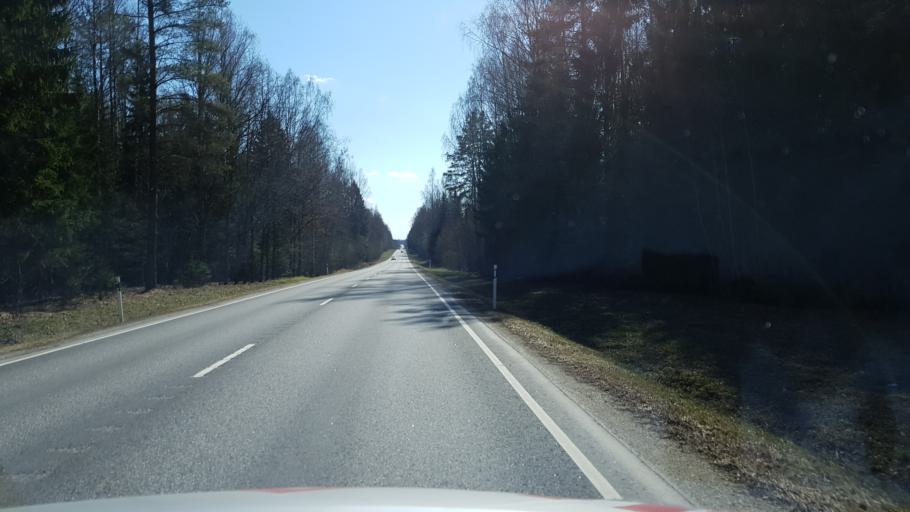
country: EE
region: Jogevamaa
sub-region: Mustvee linn
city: Mustvee
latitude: 58.6961
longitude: 26.8151
